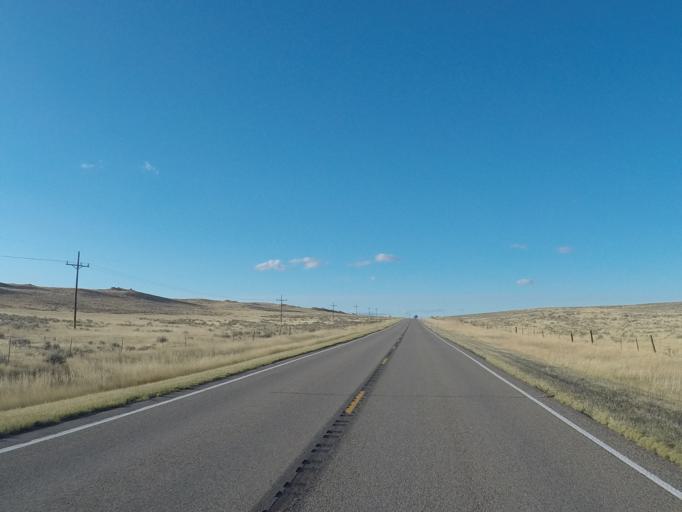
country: US
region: Montana
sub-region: Golden Valley County
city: Ryegate
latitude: 46.2356
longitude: -108.9339
